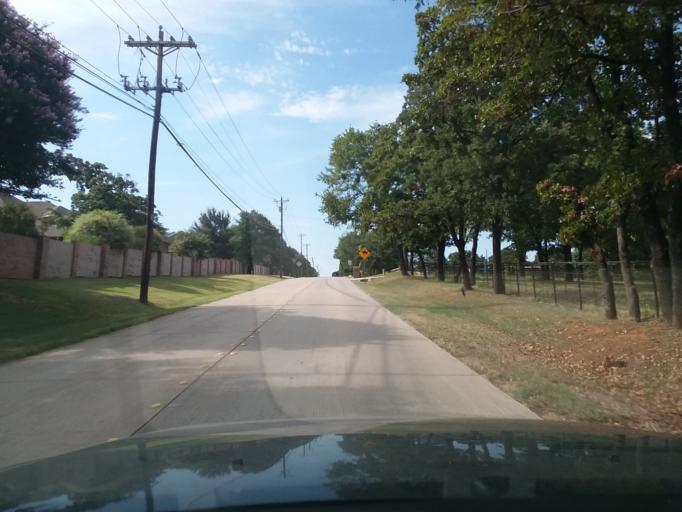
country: US
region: Texas
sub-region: Denton County
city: Double Oak
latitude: 33.0544
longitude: -97.1097
